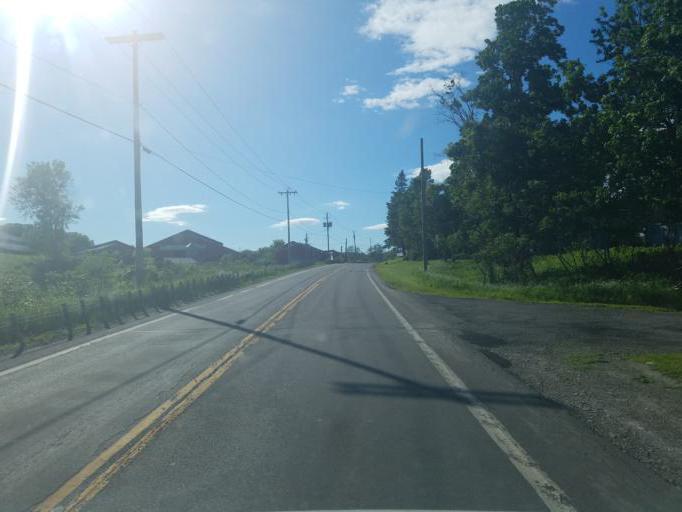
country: US
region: New York
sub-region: Herkimer County
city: Little Falls
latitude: 43.0099
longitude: -74.7966
